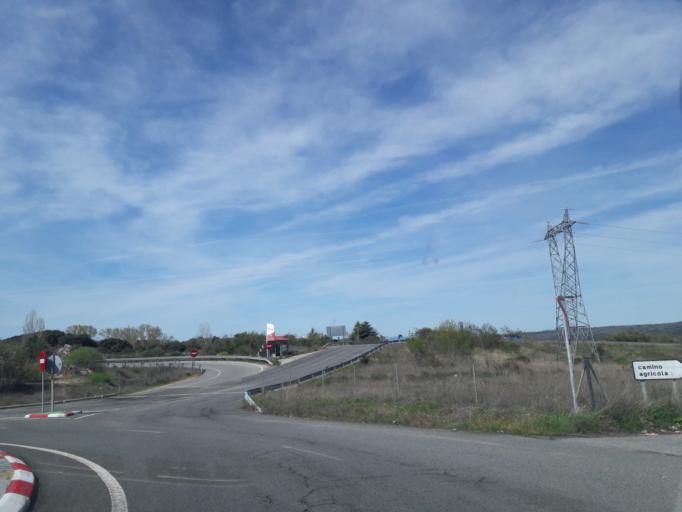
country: ES
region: Castille and Leon
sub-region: Provincia de Salamanca
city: Fuentes de Bejar
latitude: 40.4982
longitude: -5.6739
